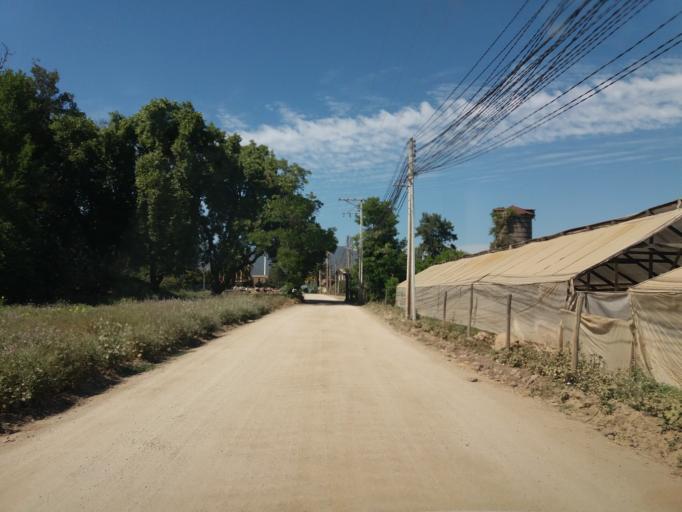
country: CL
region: Valparaiso
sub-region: Provincia de Quillota
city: Quillota
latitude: -32.8756
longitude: -71.2252
